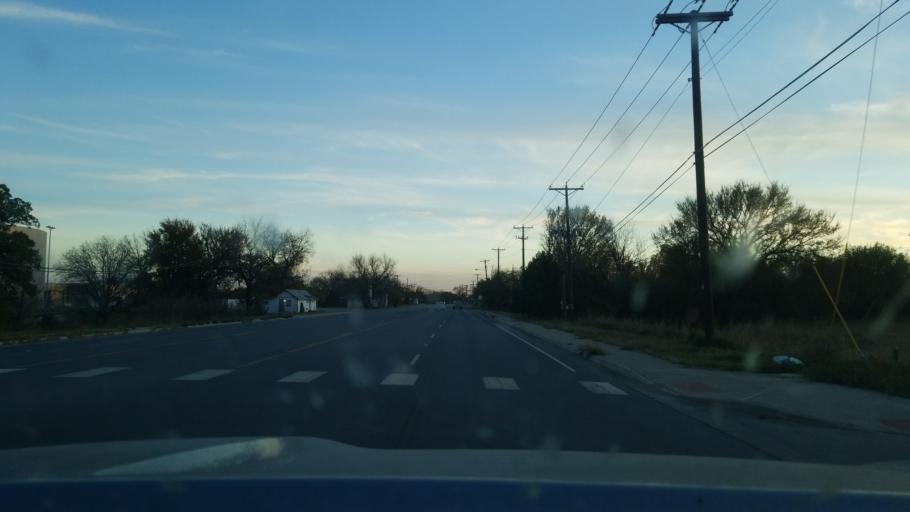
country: US
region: Texas
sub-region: Stephens County
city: Breckenridge
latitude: 32.7519
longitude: -98.9027
